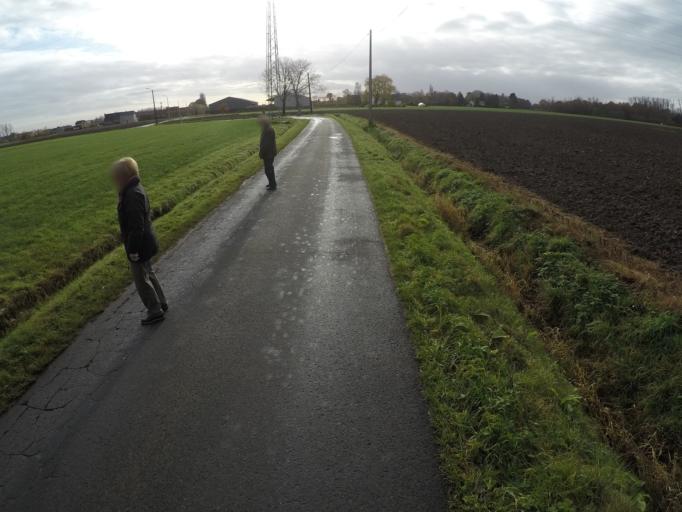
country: BE
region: Flanders
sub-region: Provincie Vlaams-Brabant
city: Londerzeel
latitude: 51.0223
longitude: 4.3050
